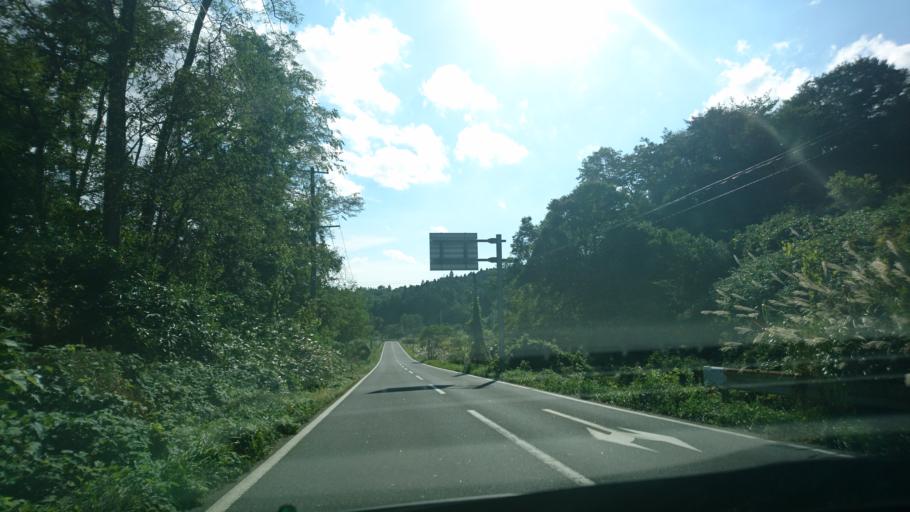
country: JP
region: Iwate
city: Ichinoseki
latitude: 38.8773
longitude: 141.1182
